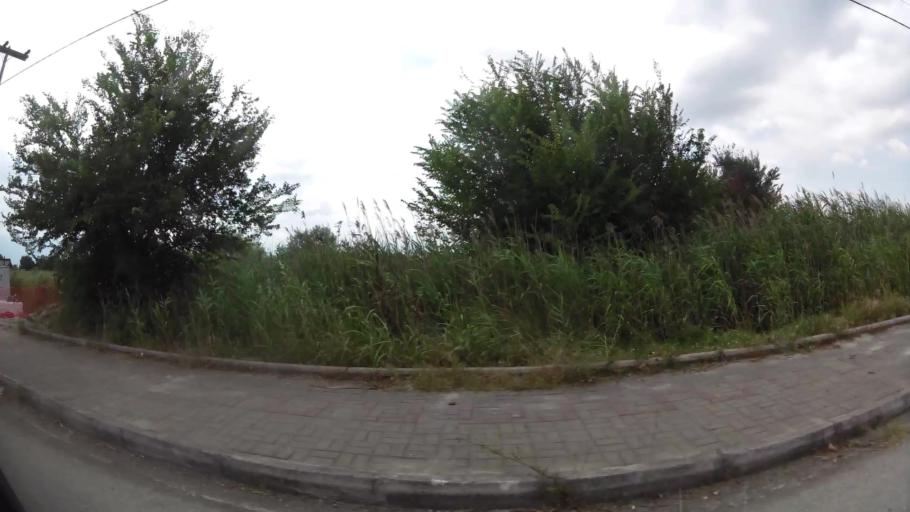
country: GR
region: Central Macedonia
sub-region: Nomos Pierias
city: Paralia
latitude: 40.2717
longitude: 22.5948
